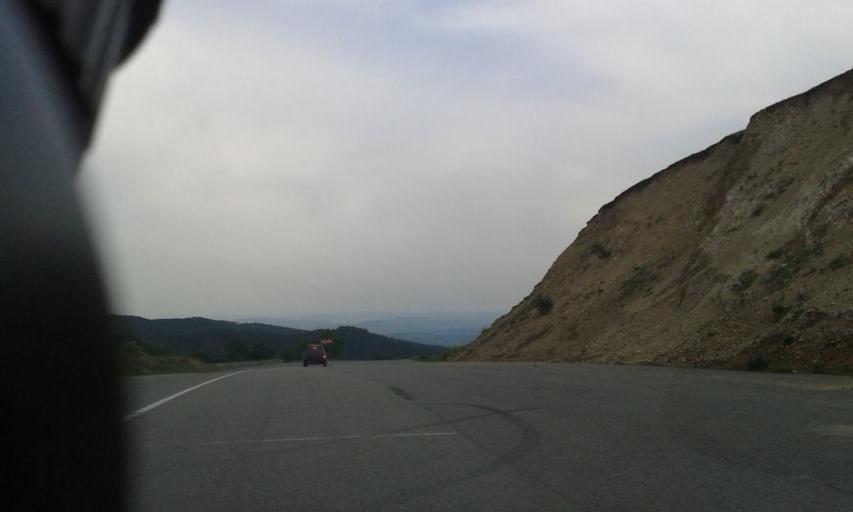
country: RO
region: Gorj
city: Novaci-Straini
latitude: 45.2275
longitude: 23.6928
